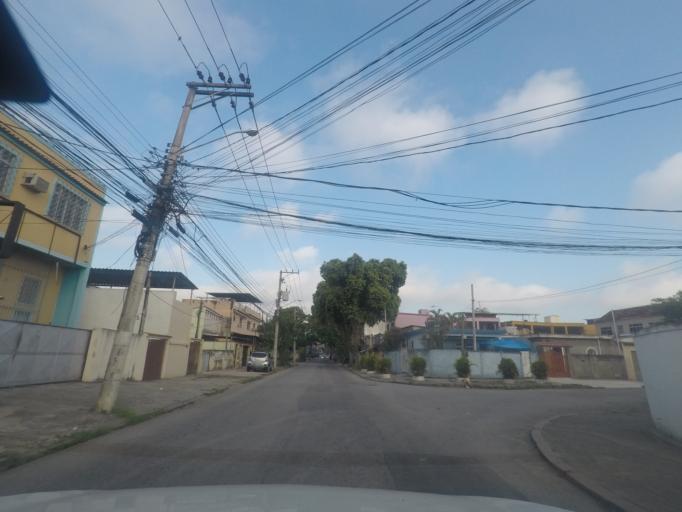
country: BR
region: Rio de Janeiro
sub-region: Duque De Caxias
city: Duque de Caxias
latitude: -22.8323
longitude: -43.2774
